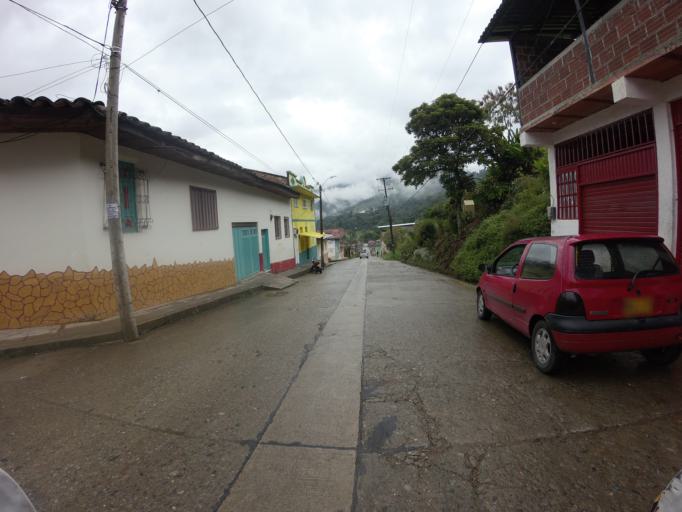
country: CO
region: Quindio
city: Genova
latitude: 4.2072
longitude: -75.7888
